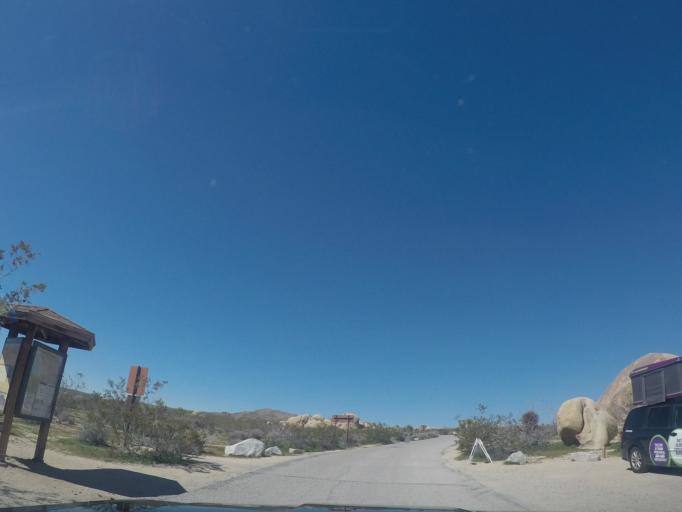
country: US
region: California
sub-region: San Bernardino County
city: Twentynine Palms
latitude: 33.9841
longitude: -116.0167
